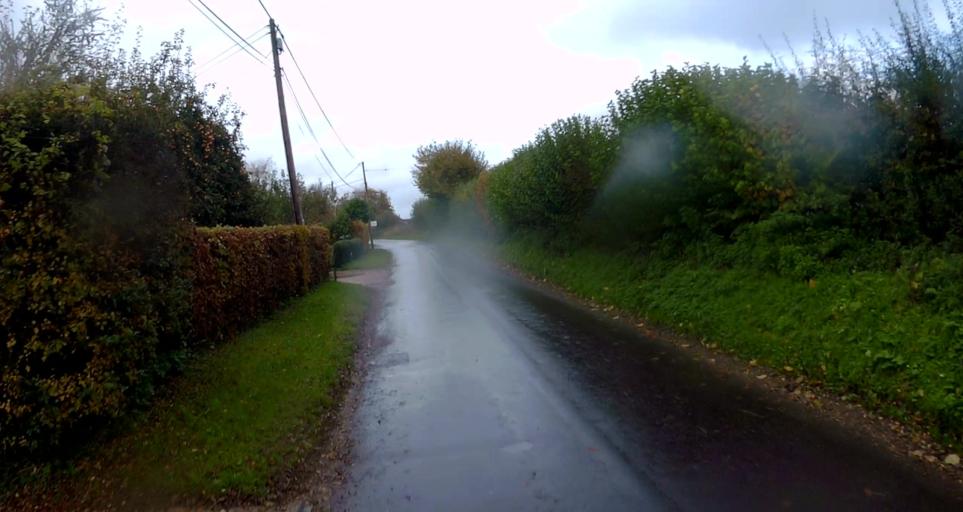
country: GB
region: England
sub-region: Hampshire
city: Four Marks
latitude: 51.1593
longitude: -1.0516
